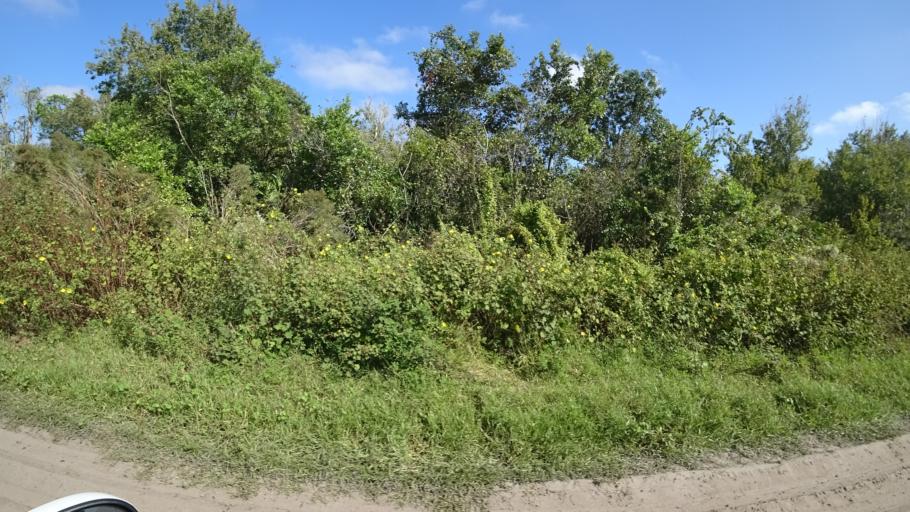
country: US
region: Florida
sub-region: DeSoto County
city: Arcadia
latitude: 27.2862
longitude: -82.0788
